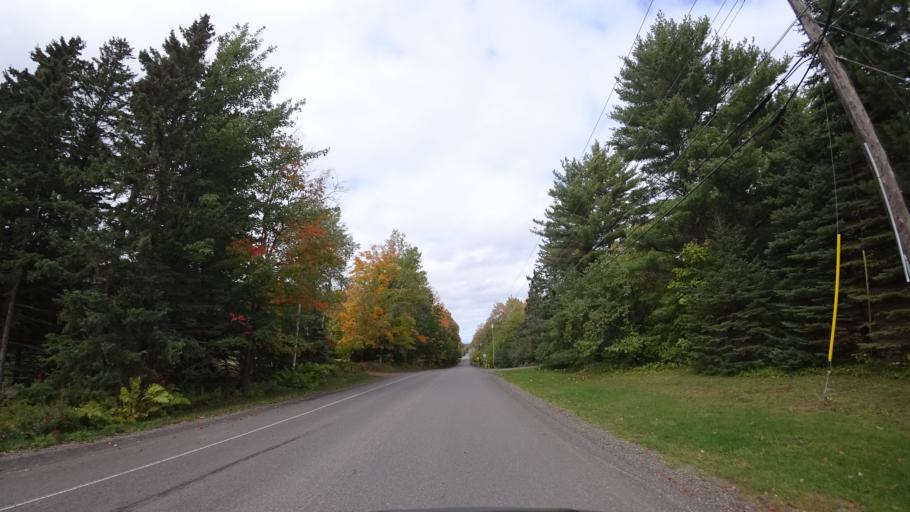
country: US
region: Michigan
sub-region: Marquette County
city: Trowbridge Park
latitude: 46.5357
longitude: -87.4375
